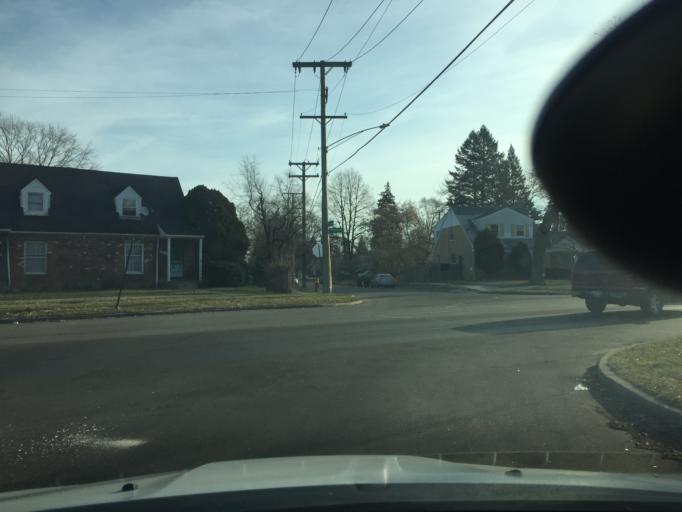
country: US
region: Michigan
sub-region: Macomb County
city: Eastpointe
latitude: 42.4340
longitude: -82.9611
